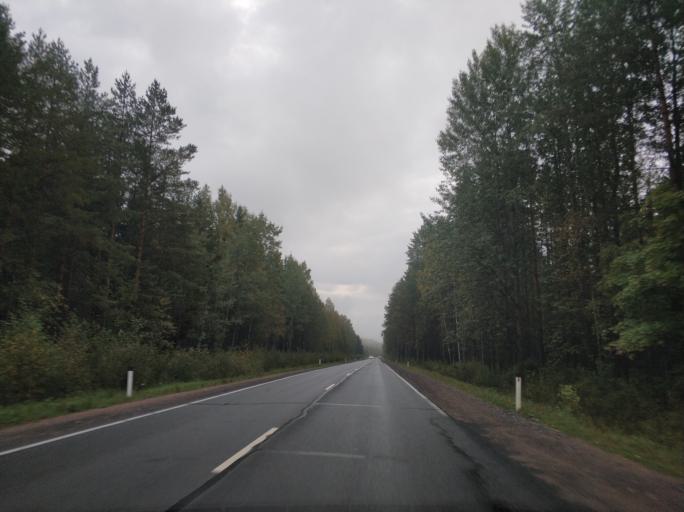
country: RU
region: Leningrad
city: Shcheglovo
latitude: 60.1021
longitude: 30.8233
